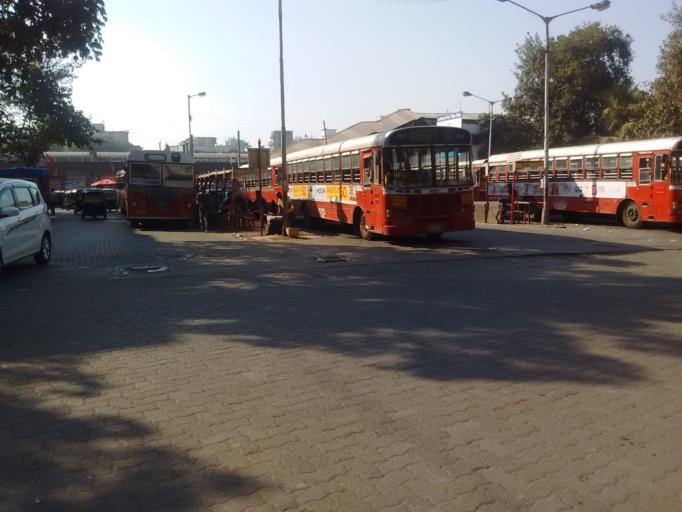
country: IN
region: Maharashtra
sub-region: Mumbai Suburban
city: Mumbai
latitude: 19.0811
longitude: 72.8426
